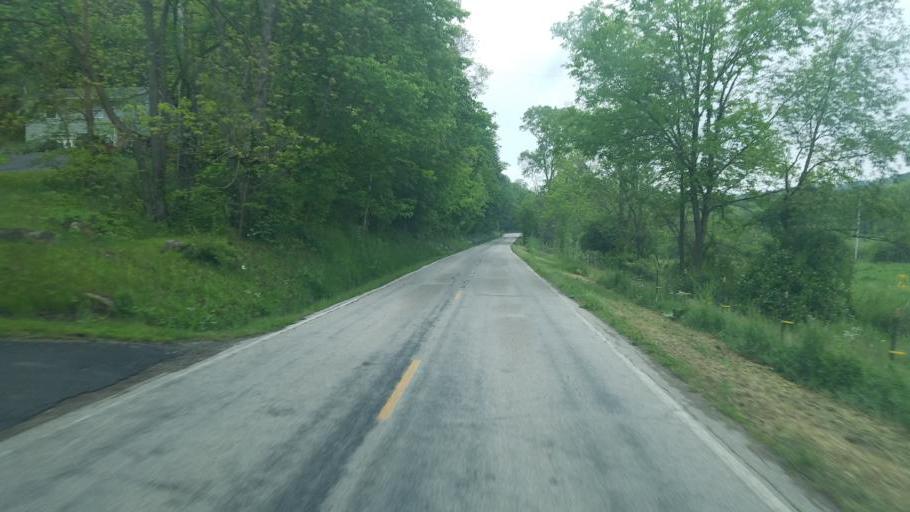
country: US
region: Ohio
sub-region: Sandusky County
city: Bellville
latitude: 40.6586
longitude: -82.4835
